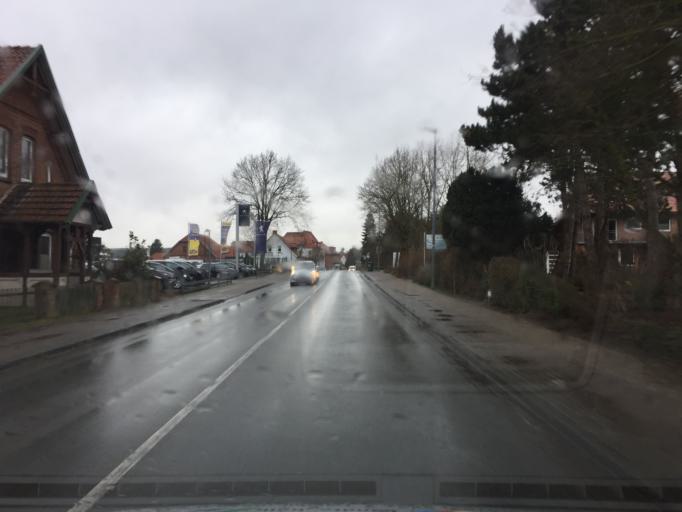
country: DE
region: Lower Saxony
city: Steyerberg
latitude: 52.5645
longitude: 9.0283
